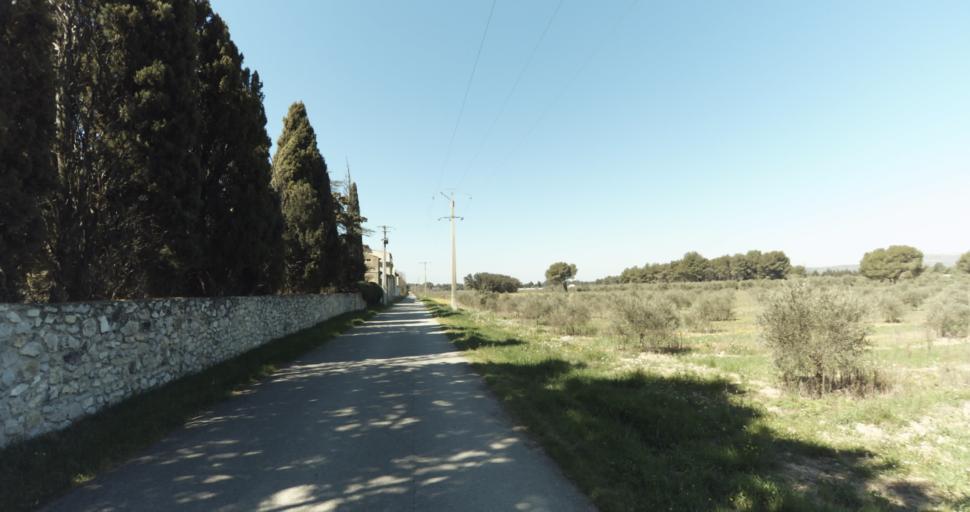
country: FR
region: Provence-Alpes-Cote d'Azur
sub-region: Departement des Bouches-du-Rhone
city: Pelissanne
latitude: 43.6114
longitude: 5.1552
